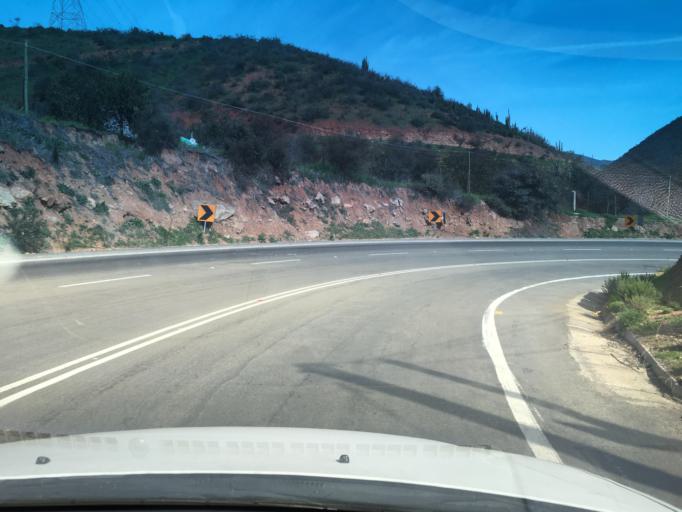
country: CL
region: Valparaiso
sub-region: Provincia de Marga Marga
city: Limache
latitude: -33.0607
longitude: -71.0540
